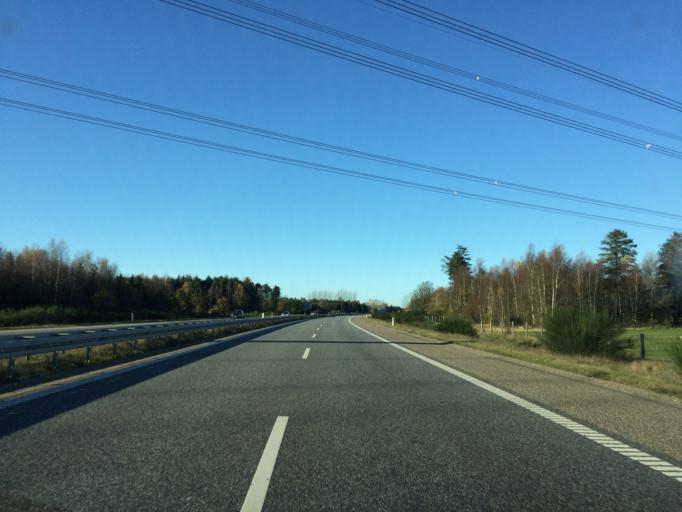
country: DK
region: Central Jutland
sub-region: Ikast-Brande Kommune
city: Brande
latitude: 55.9168
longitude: 9.1743
